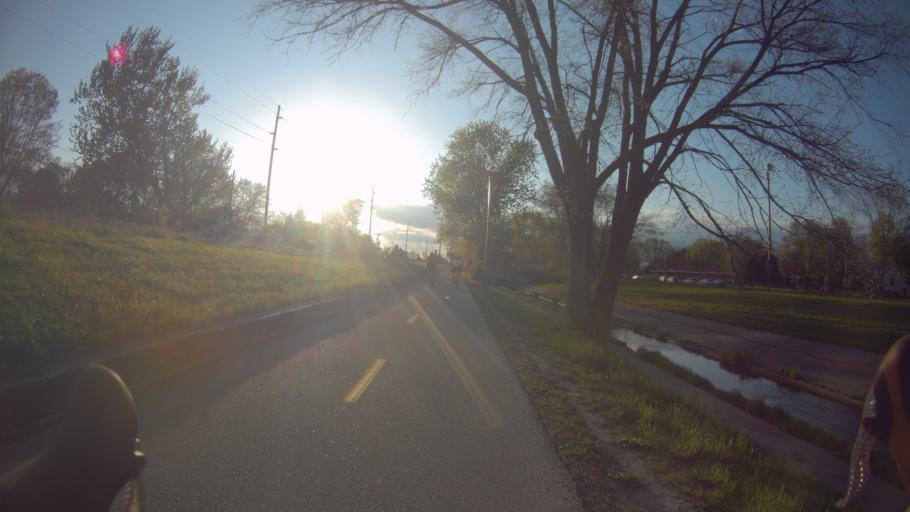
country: US
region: Wisconsin
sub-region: Dane County
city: Monona
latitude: 43.0896
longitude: -89.3239
